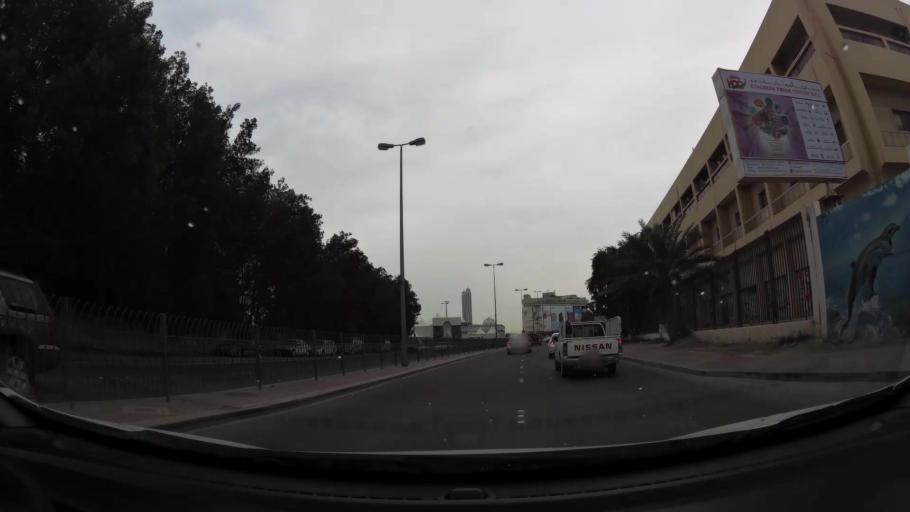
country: BH
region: Manama
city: Jidd Hafs
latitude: 26.2051
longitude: 50.5342
